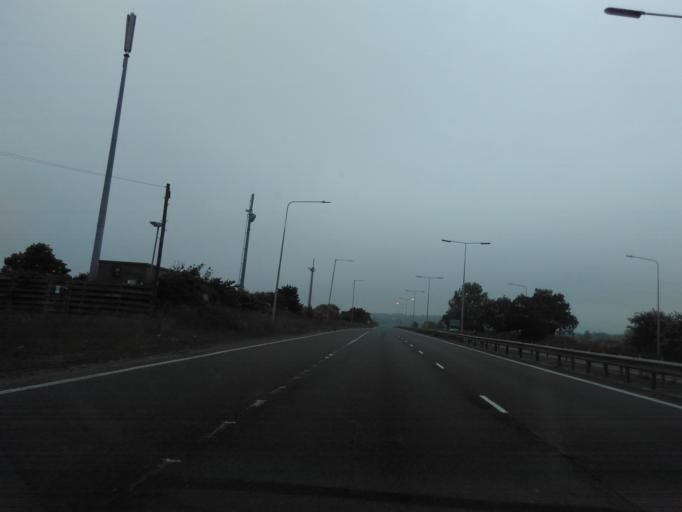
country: GB
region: England
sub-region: Kent
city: Dunkirk
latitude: 51.3263
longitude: 0.9880
